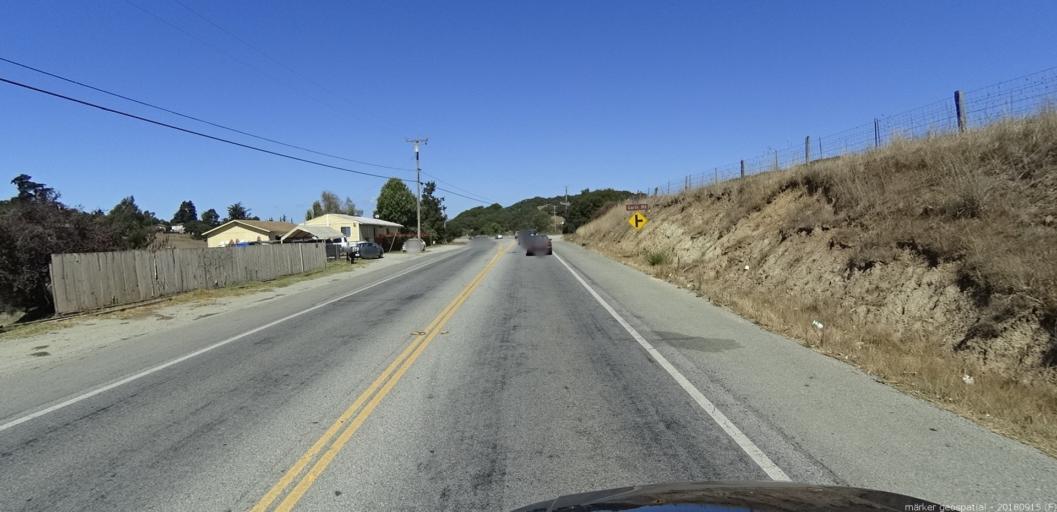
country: US
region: California
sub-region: Monterey County
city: Las Lomas
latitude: 36.8719
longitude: -121.7444
